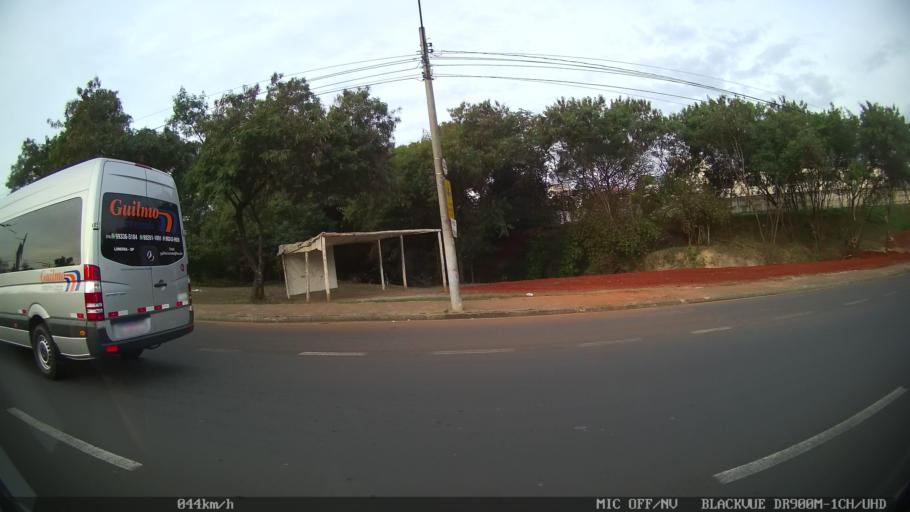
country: BR
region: Sao Paulo
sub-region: Limeira
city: Limeira
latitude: -22.5620
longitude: -47.3806
